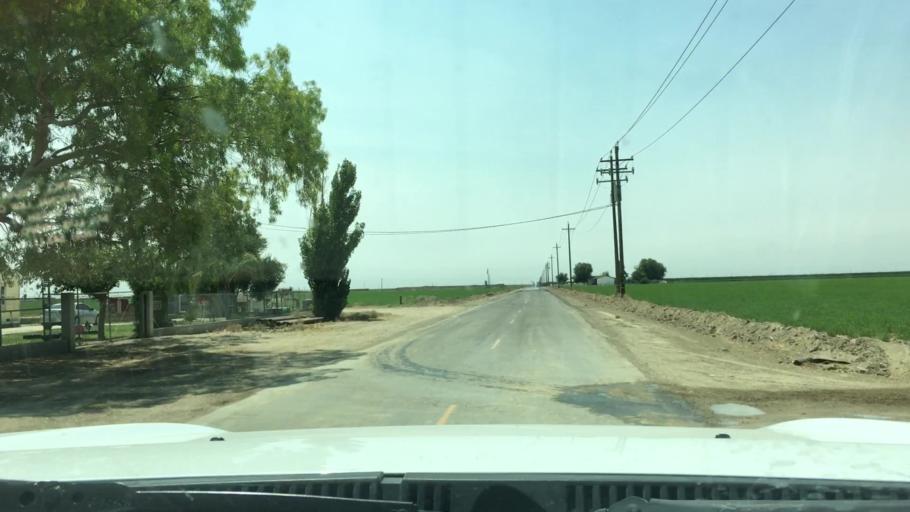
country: US
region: California
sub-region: Tulare County
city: Alpaugh
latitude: 35.7362
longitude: -119.4371
